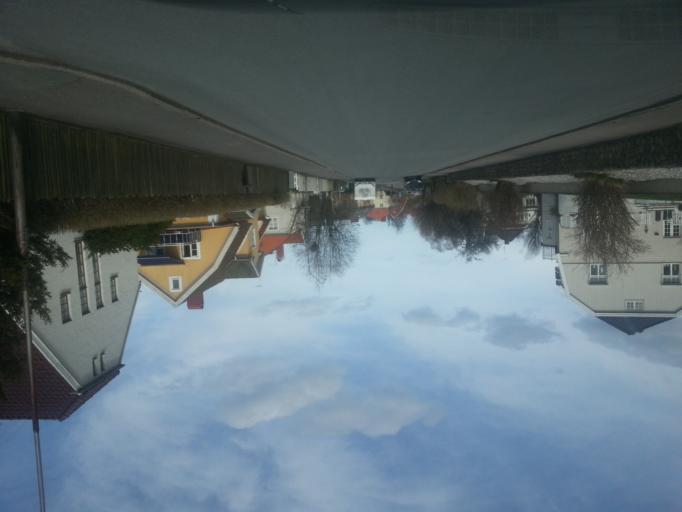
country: SE
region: Joenkoeping
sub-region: Jonkopings Kommun
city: Jonkoping
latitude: 57.7820
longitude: 14.1458
